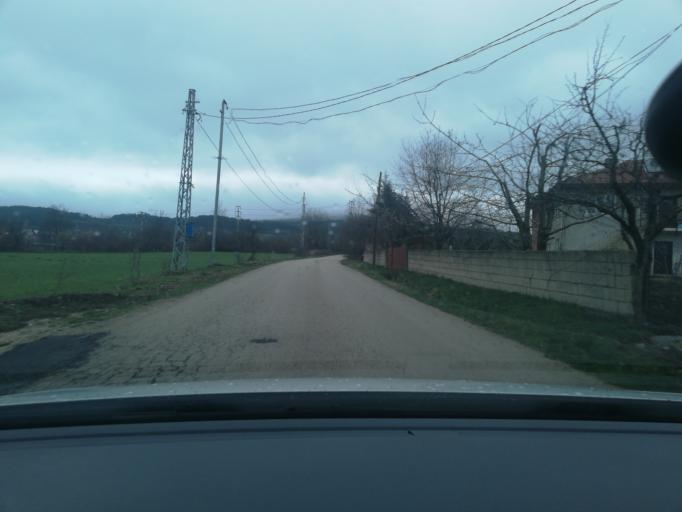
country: TR
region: Bolu
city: Bolu
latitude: 40.7312
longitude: 31.5447
